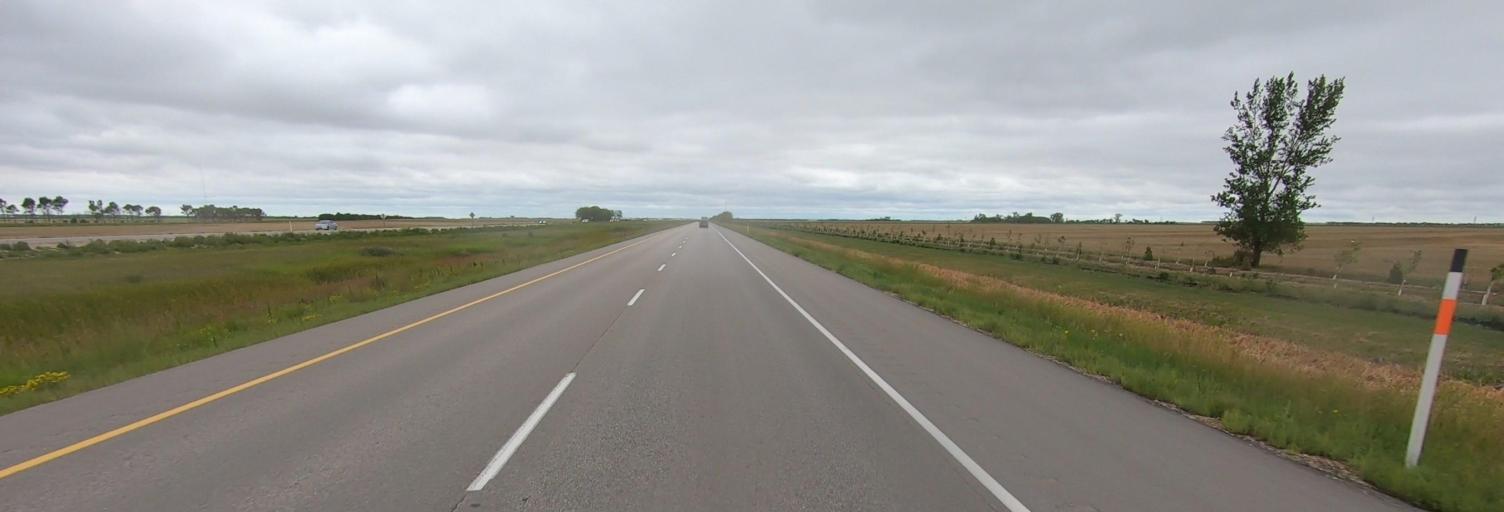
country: CA
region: Manitoba
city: Headingley
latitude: 49.8879
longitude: -97.6547
